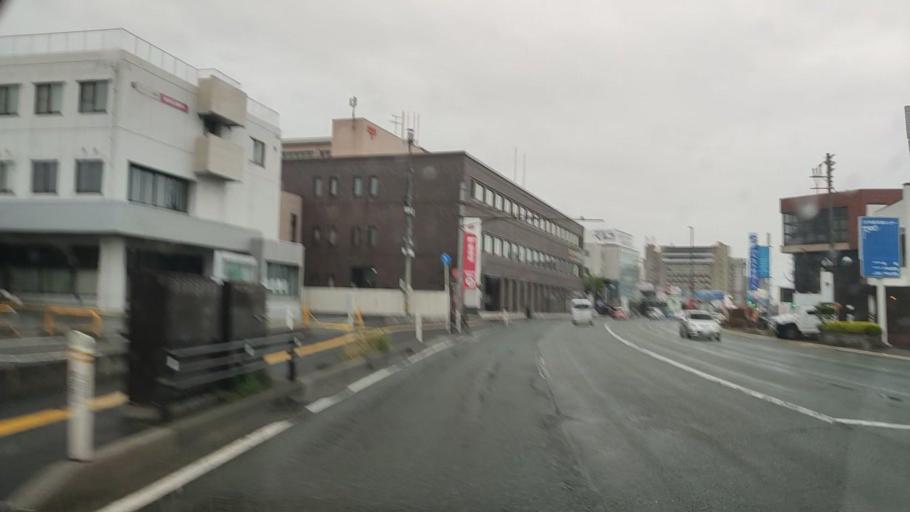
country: JP
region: Akita
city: Akita Shi
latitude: 39.7241
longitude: 140.1087
